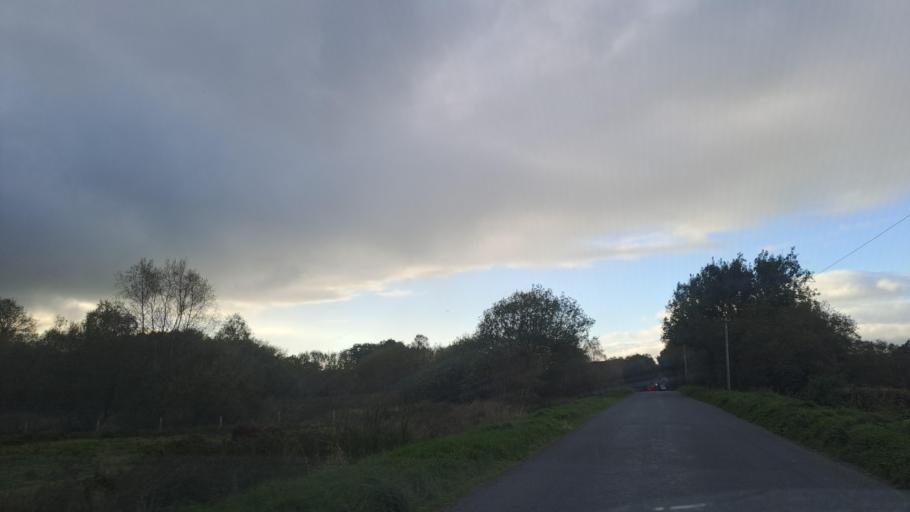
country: IE
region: Ulster
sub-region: County Monaghan
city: Castleblayney
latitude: 54.0373
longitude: -6.8213
